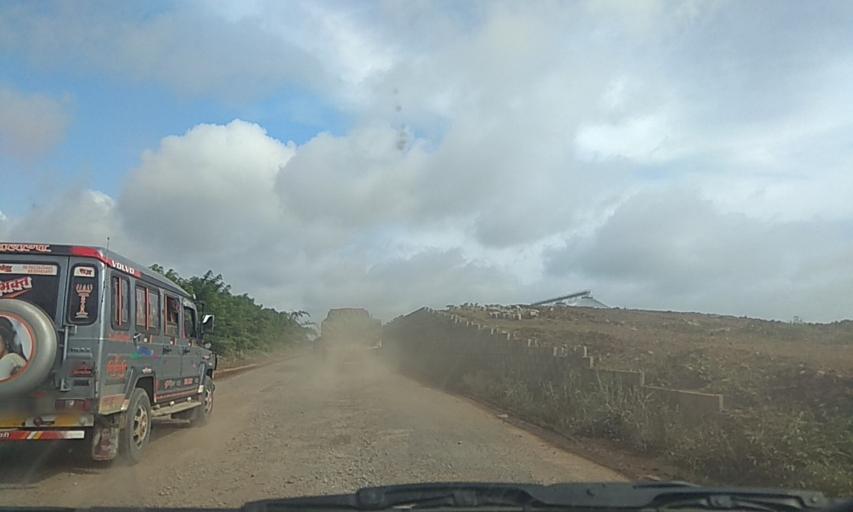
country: IN
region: Karnataka
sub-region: Haveri
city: Shiggaon
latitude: 15.0397
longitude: 75.1721
